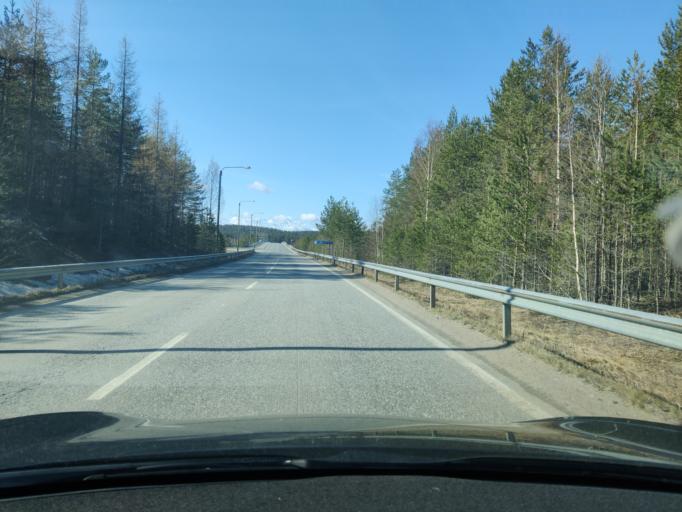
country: FI
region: Northern Savo
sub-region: Kuopio
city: Vehmersalmi
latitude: 62.7717
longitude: 28.0093
